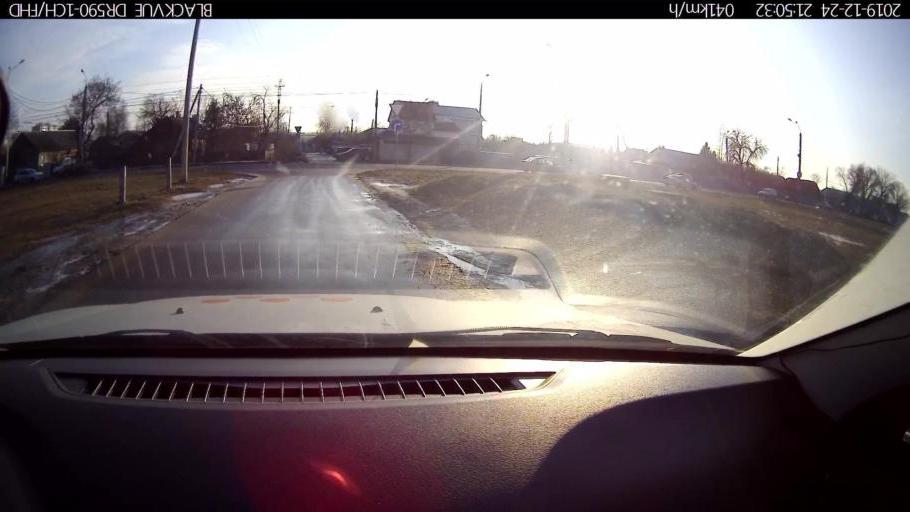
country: RU
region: Nizjnij Novgorod
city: Burevestnik
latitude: 56.2211
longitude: 43.8456
